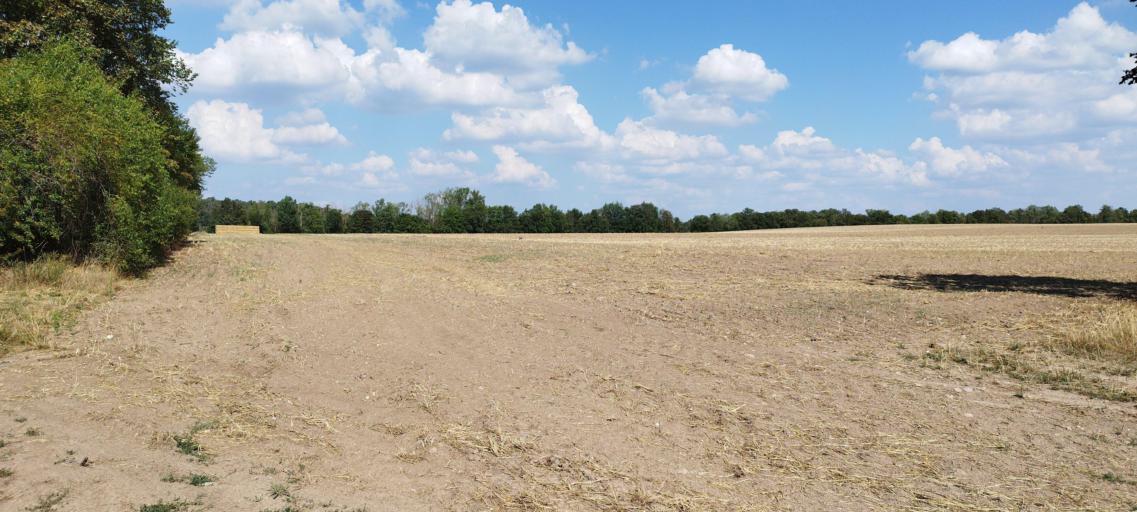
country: DE
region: Brandenburg
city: Wiesenburg
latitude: 52.1381
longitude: 12.5060
